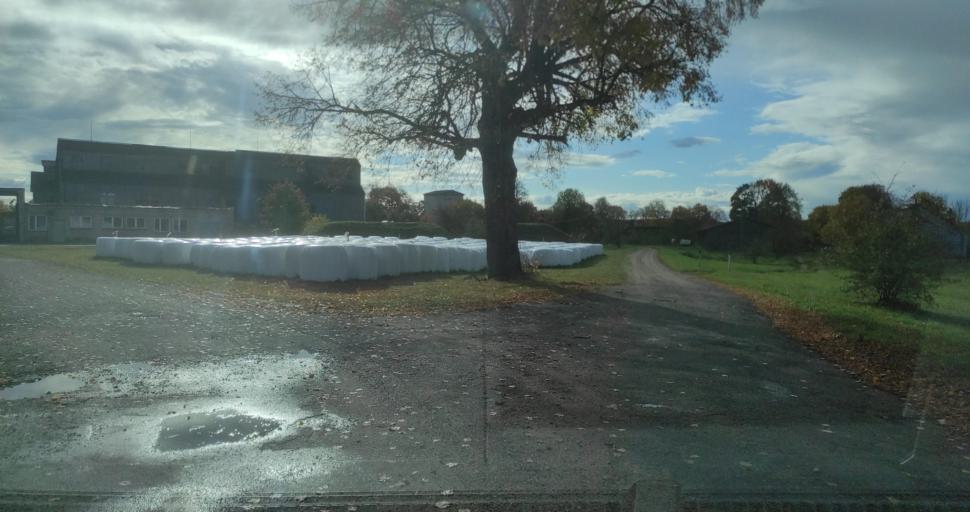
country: LV
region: Vainode
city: Vainode
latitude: 56.5683
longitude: 21.9008
